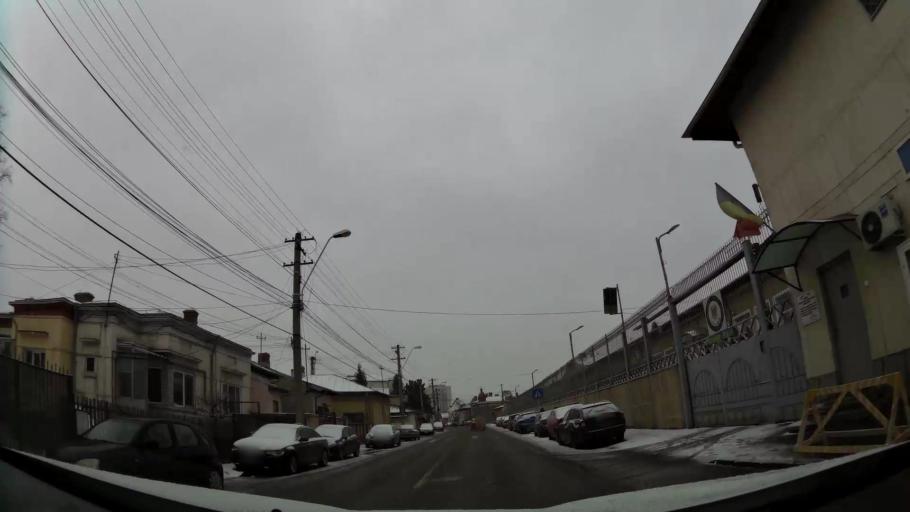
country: RO
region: Prahova
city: Ploiesti
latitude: 44.9331
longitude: 26.0202
